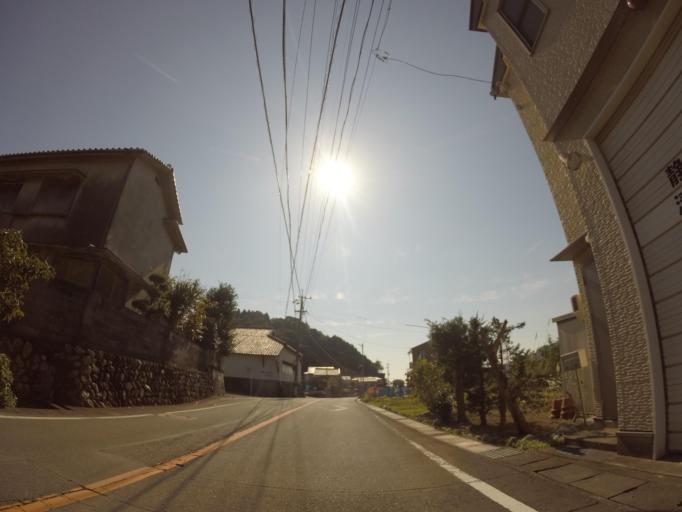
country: JP
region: Shizuoka
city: Fujinomiya
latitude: 35.0710
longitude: 138.5273
